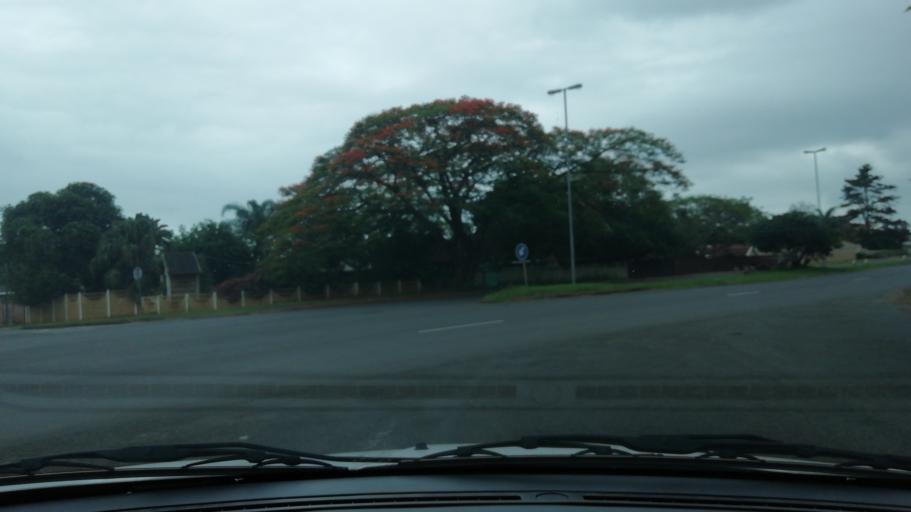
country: ZA
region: KwaZulu-Natal
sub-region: uThungulu District Municipality
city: Empangeni
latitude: -28.7618
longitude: 31.8964
